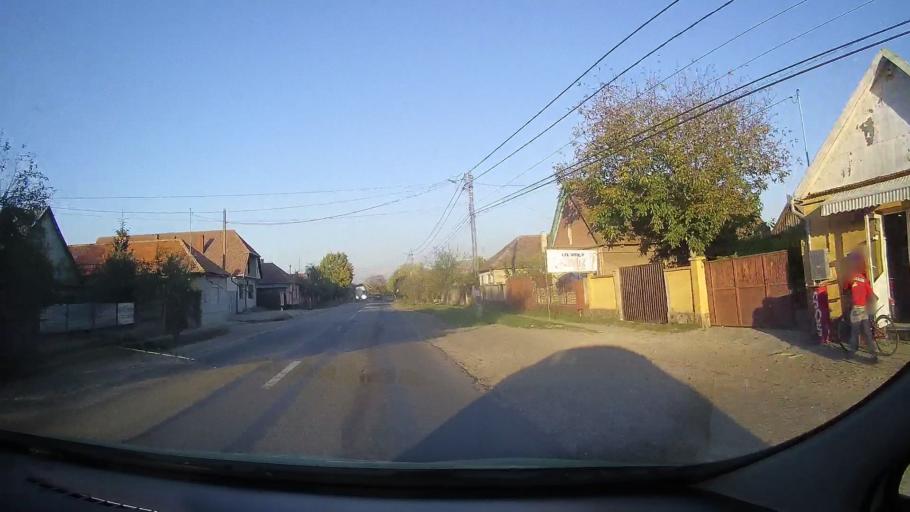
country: RO
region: Bihor
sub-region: Comuna Salard
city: Salard
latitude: 47.2194
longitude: 22.0358
